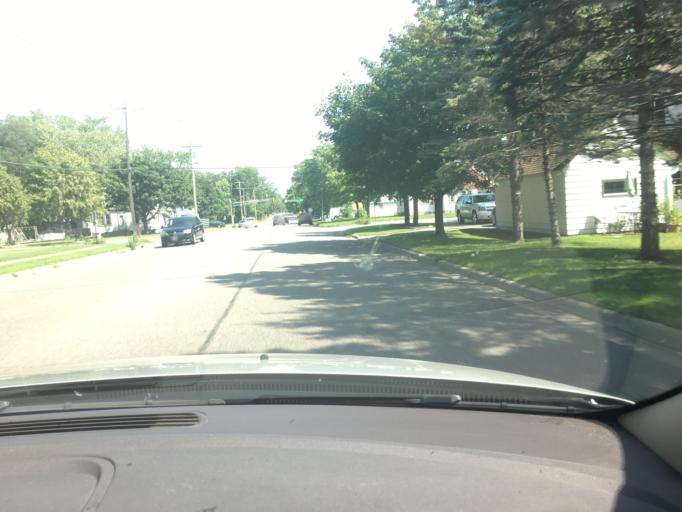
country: US
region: Minnesota
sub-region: Stearns County
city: Saint Cloud
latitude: 45.5368
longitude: -94.1643
